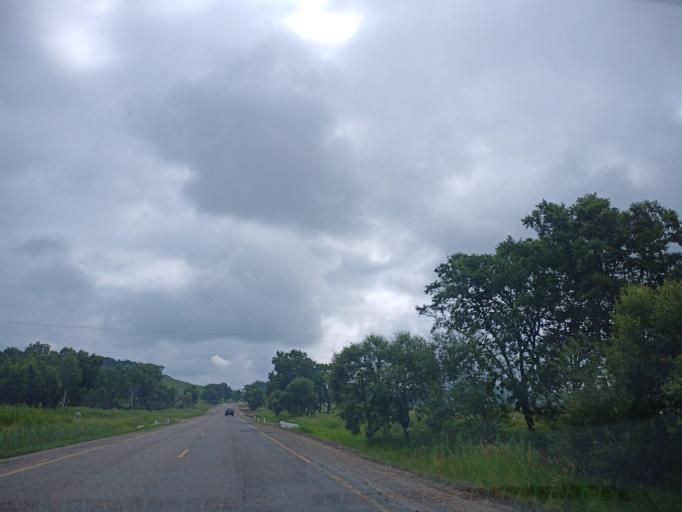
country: RU
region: Primorskiy
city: Dal'nerechensk
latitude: 46.0382
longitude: 133.8779
